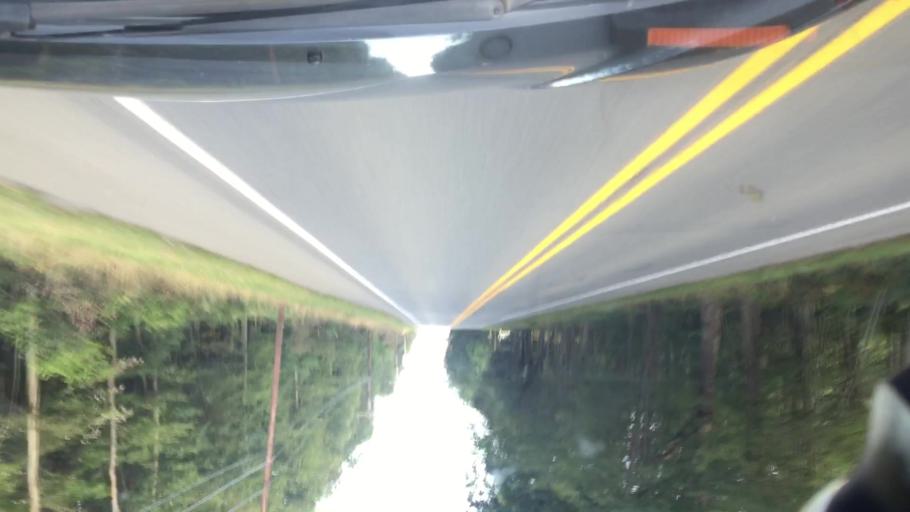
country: US
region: Pennsylvania
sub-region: Carbon County
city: Towamensing Trails
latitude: 40.9758
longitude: -75.6375
